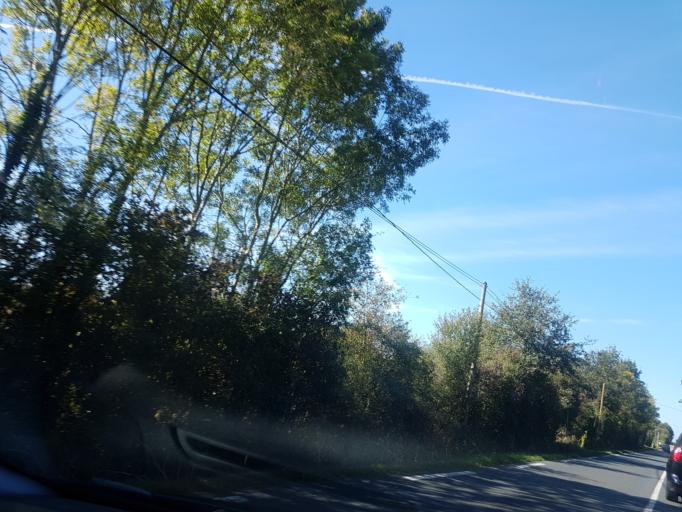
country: FR
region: Pays de la Loire
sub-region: Departement de la Loire-Atlantique
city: Casson
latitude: 47.4286
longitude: -1.5639
